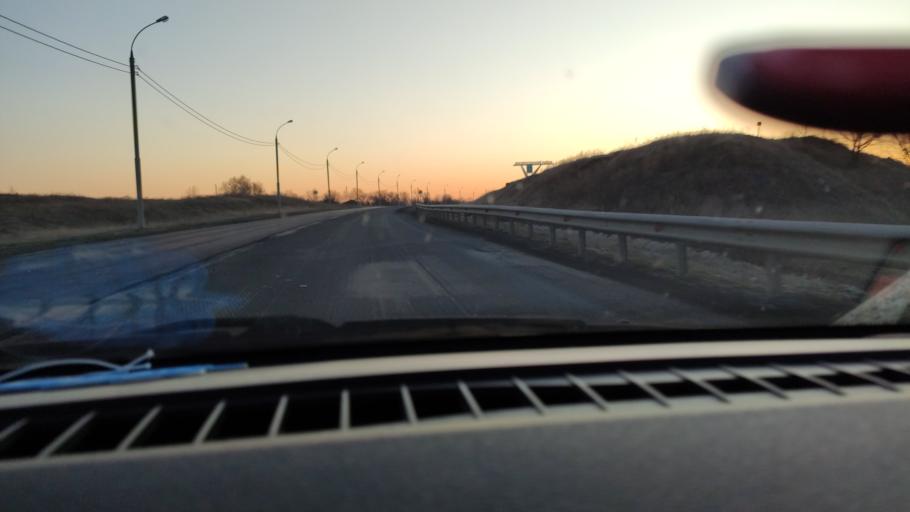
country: RU
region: Saratov
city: Yelshanka
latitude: 51.8266
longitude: 46.2225
